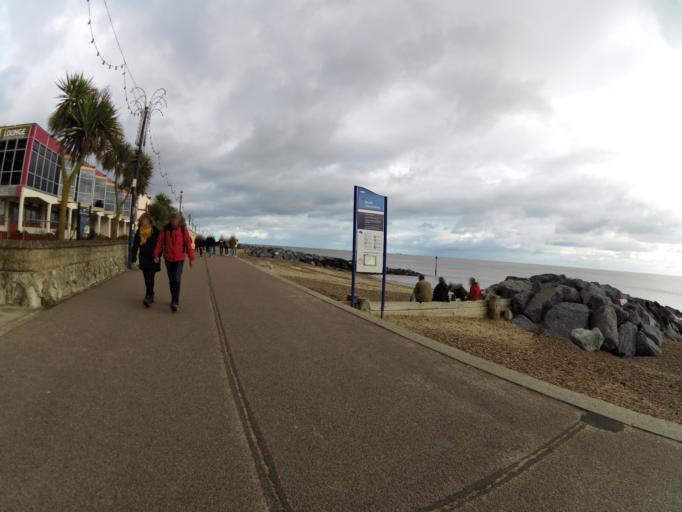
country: GB
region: England
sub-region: Suffolk
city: Felixstowe
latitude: 51.9605
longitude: 1.3543
